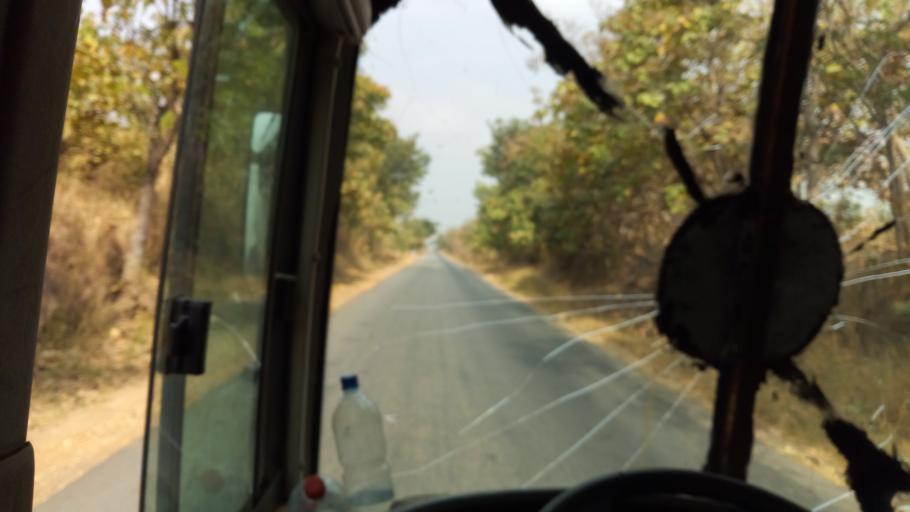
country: TG
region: Centrale
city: Sokode
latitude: 9.1682
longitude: 1.1802
